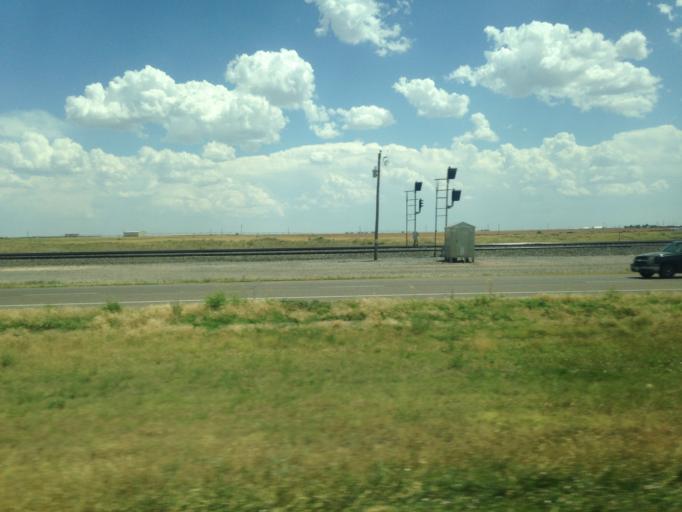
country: US
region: Texas
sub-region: Parmer County
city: Friona
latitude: 34.6467
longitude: -102.6895
